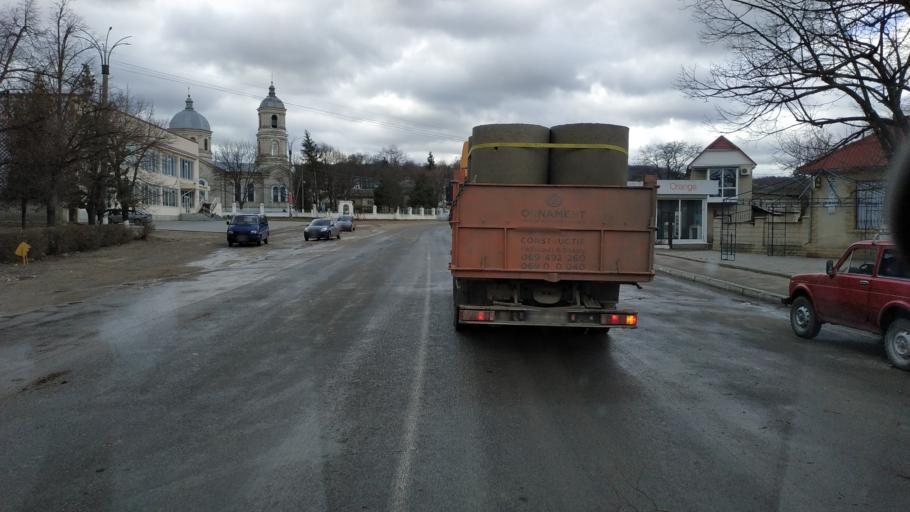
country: MD
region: Stinga Nistrului
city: Bucovat
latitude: 47.1541
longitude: 28.4278
